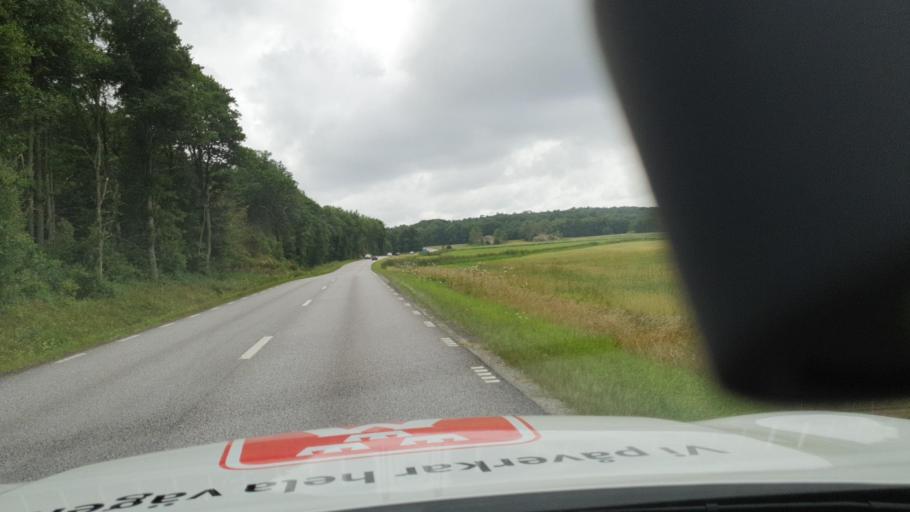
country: SE
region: Vaestra Goetaland
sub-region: Tanums Kommun
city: Grebbestad
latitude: 58.7193
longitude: 11.2737
